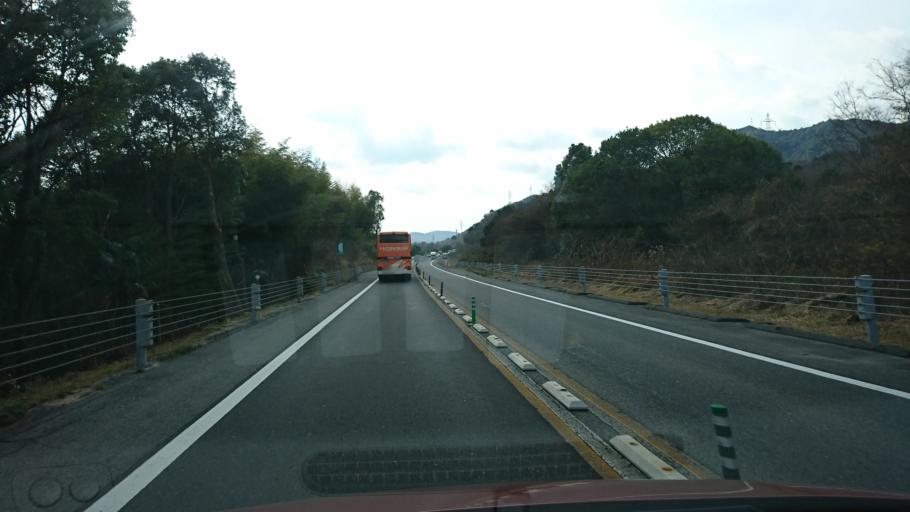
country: JP
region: Hiroshima
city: Innoshima
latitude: 34.2348
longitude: 133.0481
